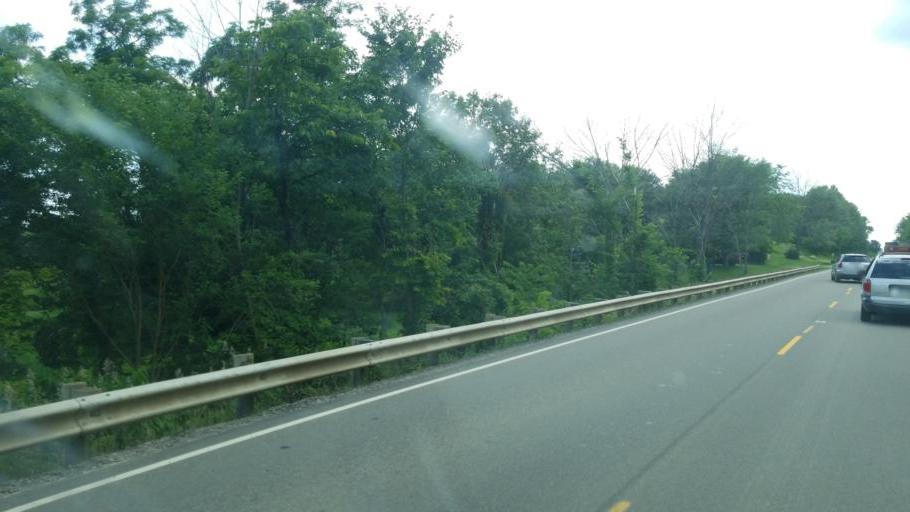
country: US
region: Ohio
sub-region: Knox County
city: Oak Hill
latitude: 40.3405
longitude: -82.1361
